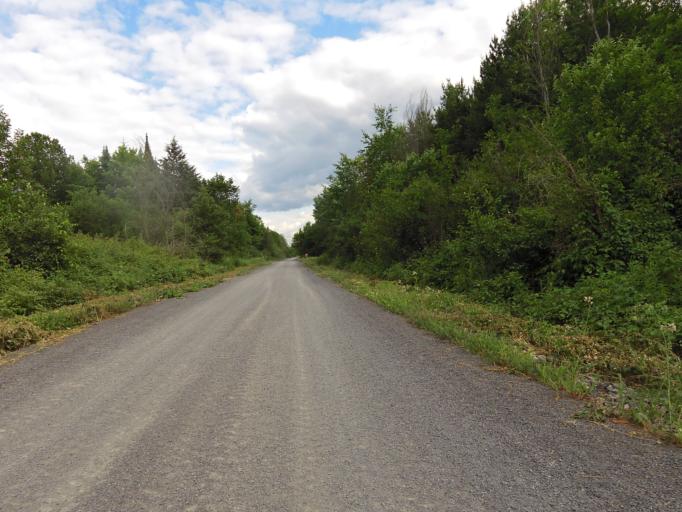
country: CA
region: Ontario
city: Carleton Place
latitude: 45.2838
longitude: -76.2475
